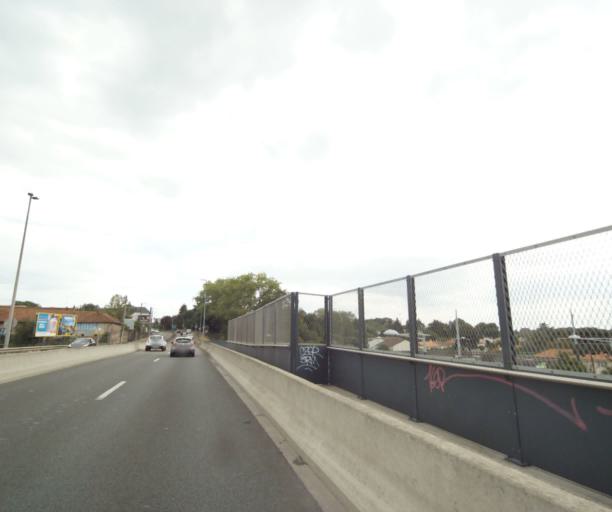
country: FR
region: Centre
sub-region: Departement du Loiret
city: Saint-Jean-de-la-Ruelle
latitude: 47.9028
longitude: 1.8719
